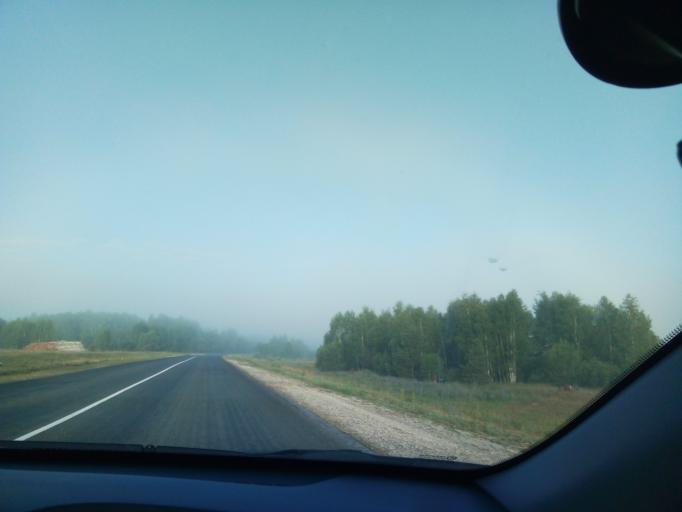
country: RU
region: Nizjnij Novgorod
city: Voznesenskoye
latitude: 54.8644
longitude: 42.9459
